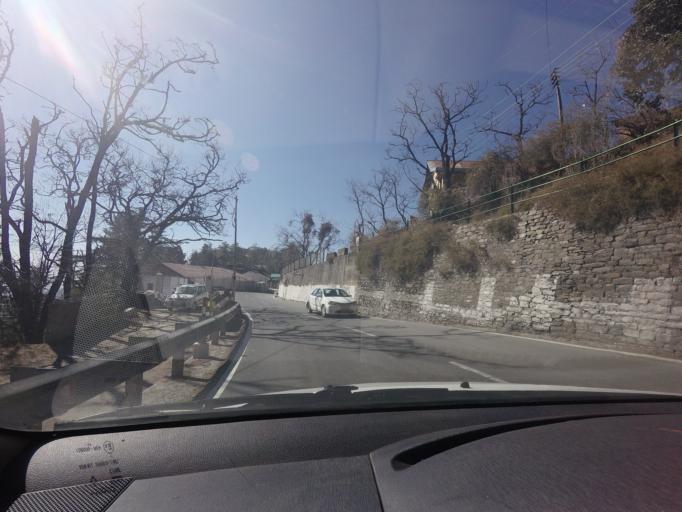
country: IN
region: Himachal Pradesh
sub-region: Shimla
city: Shimla
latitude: 31.1114
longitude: 77.2191
